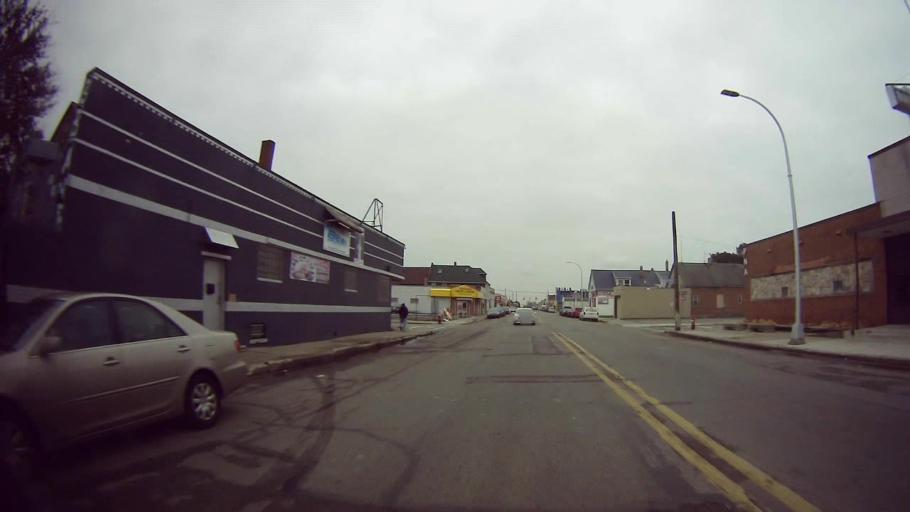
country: US
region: Michigan
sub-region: Wayne County
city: Hamtramck
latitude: 42.4014
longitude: -83.0519
